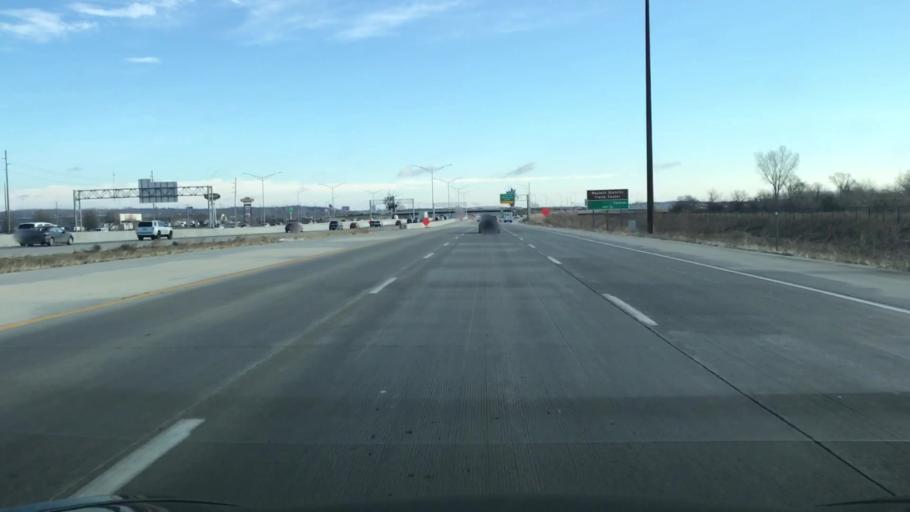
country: US
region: Iowa
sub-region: Pottawattamie County
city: Council Bluffs
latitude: 41.2322
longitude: -95.8888
